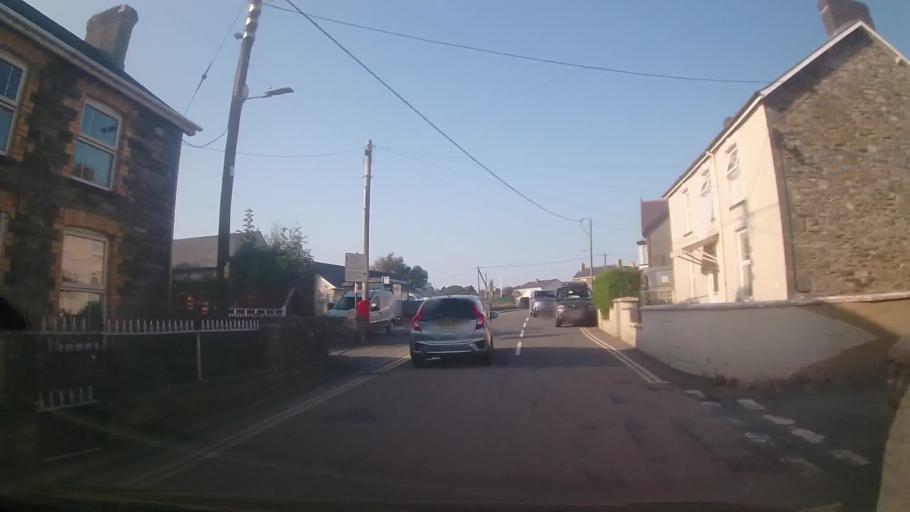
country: GB
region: Wales
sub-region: County of Ceredigion
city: Lledrod
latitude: 52.2840
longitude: -3.8626
